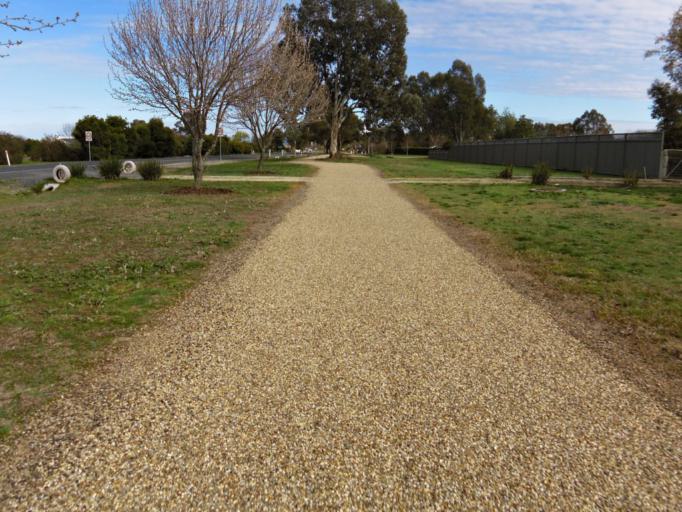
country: AU
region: Victoria
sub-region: Wangaratta
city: Wangaratta
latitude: -36.4500
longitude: 146.4362
